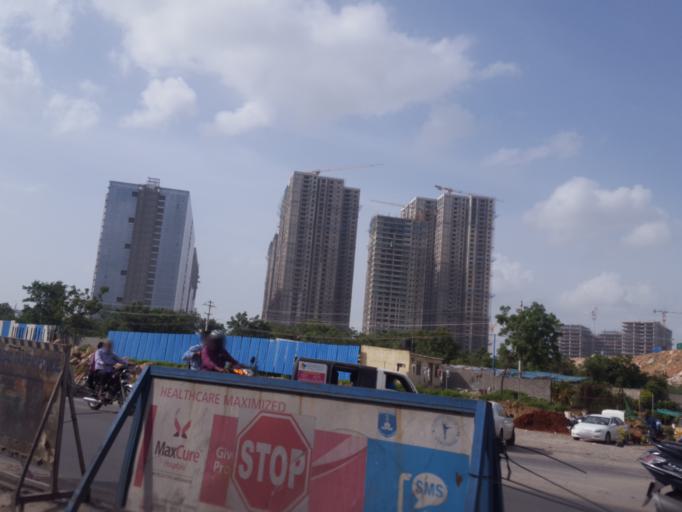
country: IN
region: Telangana
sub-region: Rangareddi
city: Kukatpalli
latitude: 17.4265
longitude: 78.3769
